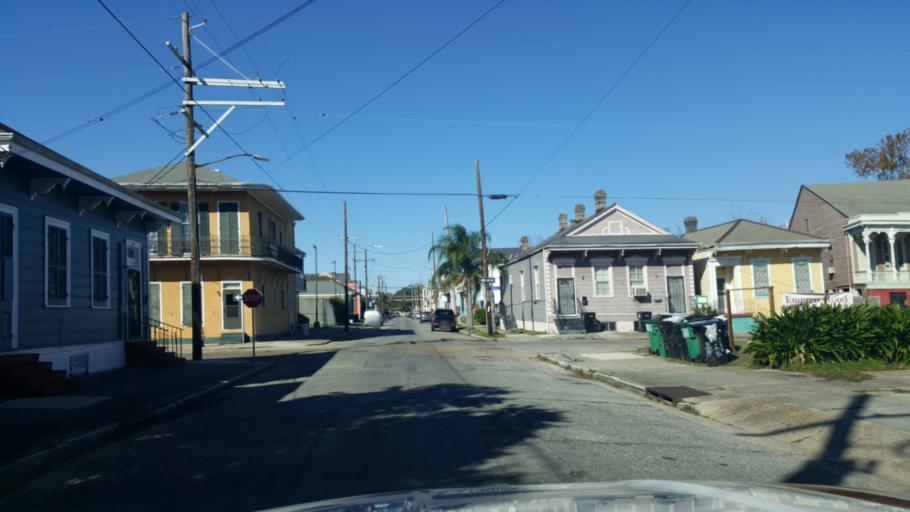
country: US
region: Louisiana
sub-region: Orleans Parish
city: New Orleans
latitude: 29.9653
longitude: -90.0678
